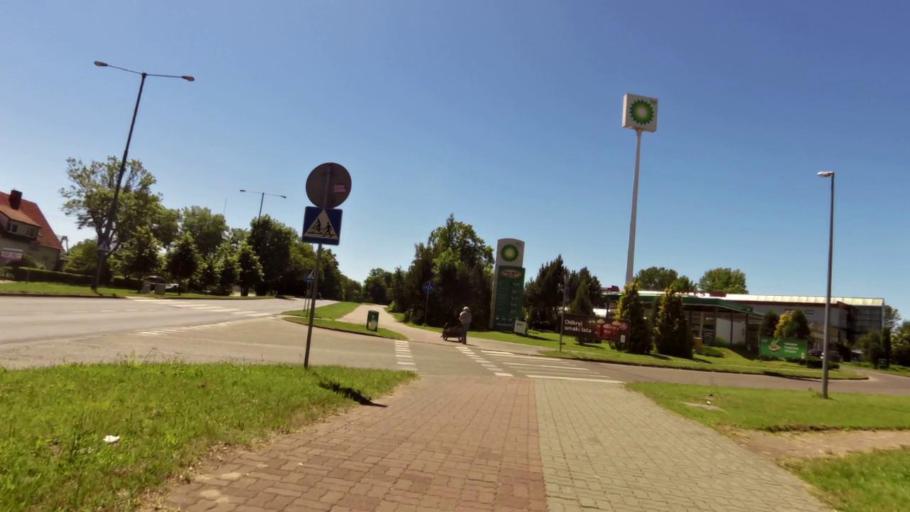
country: PL
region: West Pomeranian Voivodeship
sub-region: Powiat kolobrzeski
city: Kolobrzeg
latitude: 54.1608
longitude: 15.5662
